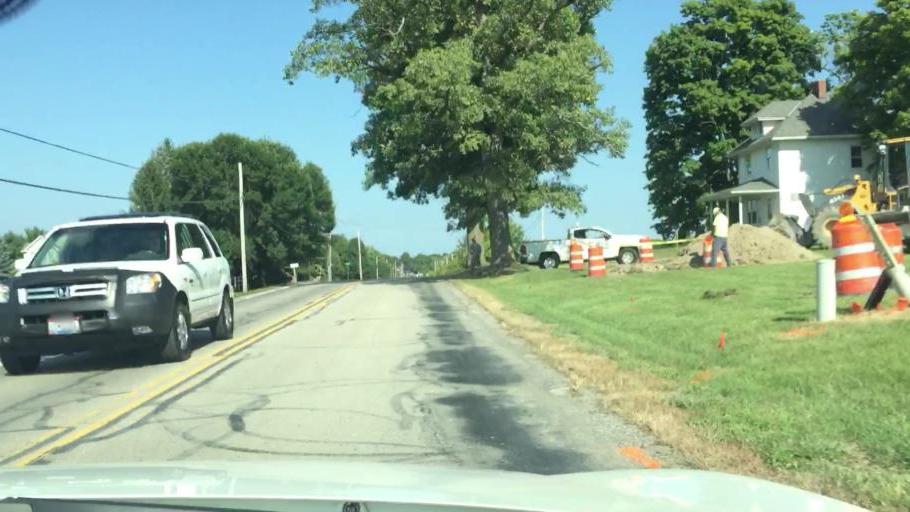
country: US
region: Ohio
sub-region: Union County
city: Marysville
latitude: 40.2283
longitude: -83.3961
